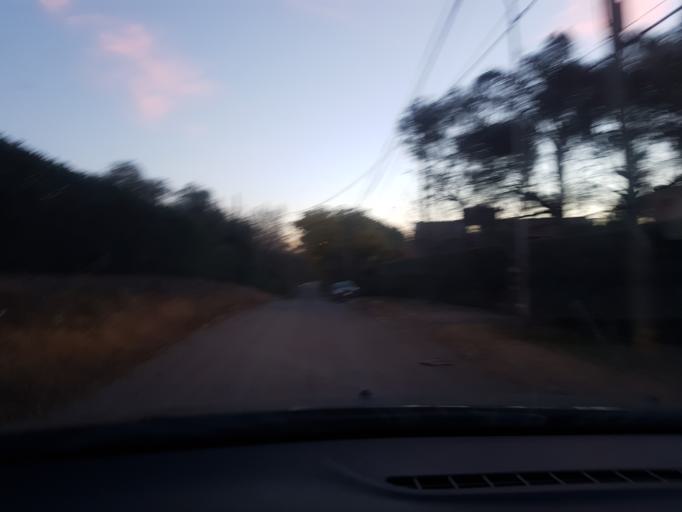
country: AR
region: Cordoba
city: Villa Allende
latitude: -31.2787
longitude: -64.2848
